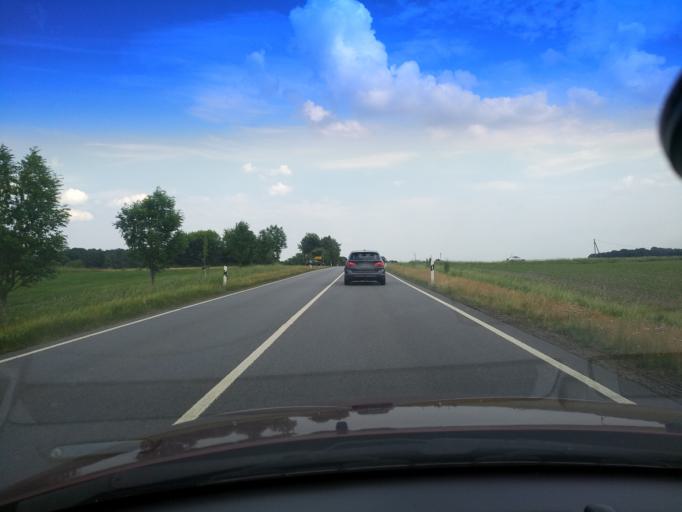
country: DE
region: Saxony
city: Niesky
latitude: 51.2683
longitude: 14.8493
